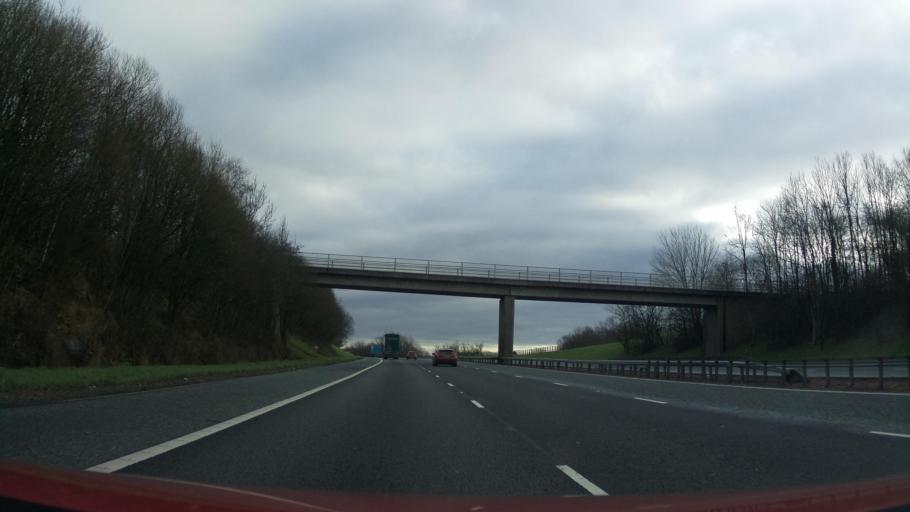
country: GB
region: Scotland
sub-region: Dumfries and Galloway
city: Annan
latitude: 55.0350
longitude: -3.1720
